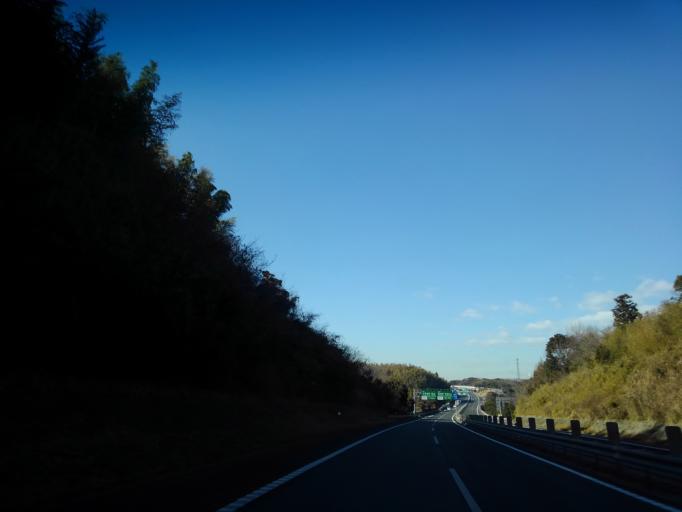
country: JP
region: Chiba
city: Kisarazu
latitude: 35.3499
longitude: 139.9301
